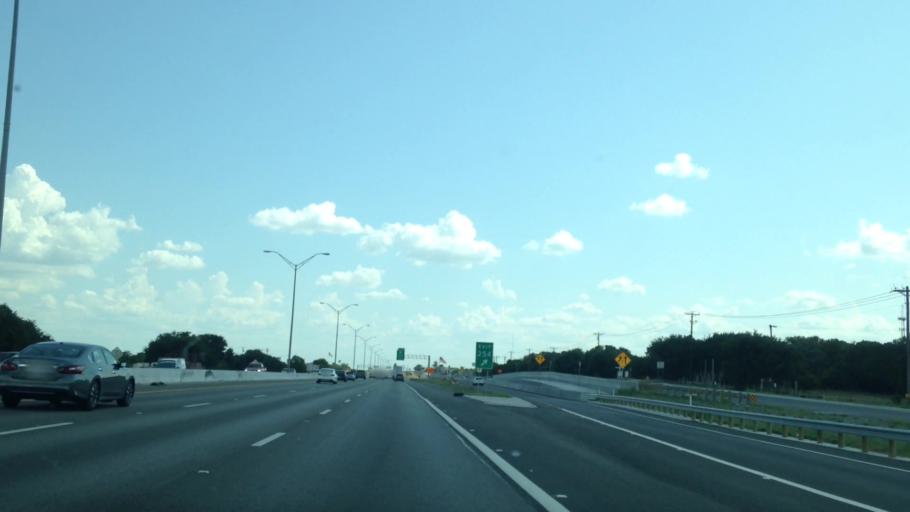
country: US
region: Texas
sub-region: Williamson County
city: Round Rock
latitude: 30.5522
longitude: -97.6926
